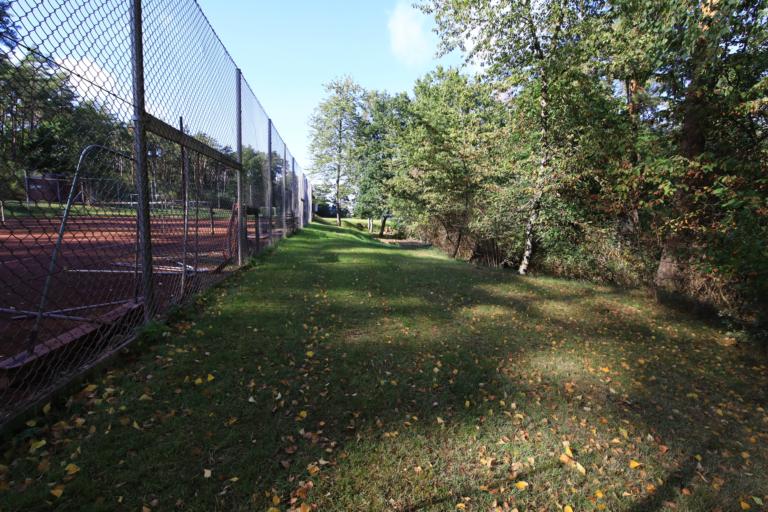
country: SE
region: Halland
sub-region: Varbergs Kommun
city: Varberg
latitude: 57.1779
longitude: 12.2203
